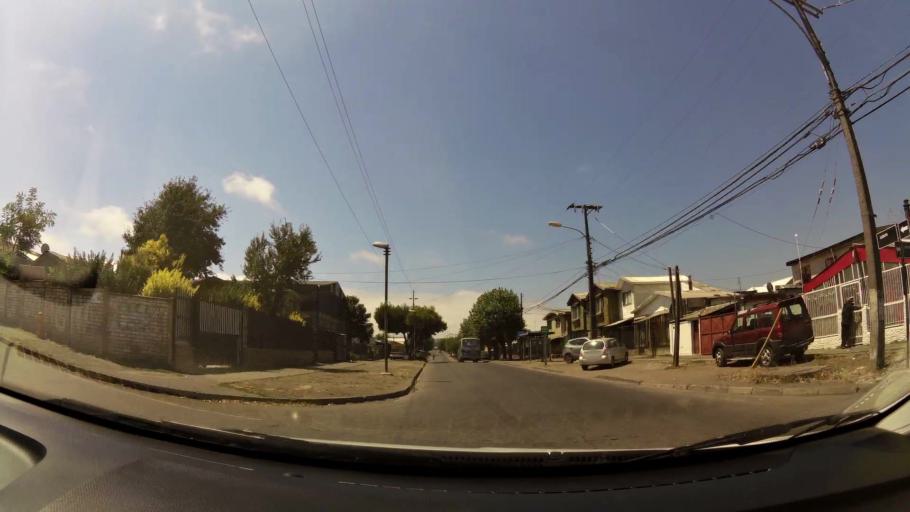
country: CL
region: Biobio
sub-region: Provincia de Concepcion
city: Concepcion
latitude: -36.8080
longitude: -73.0468
